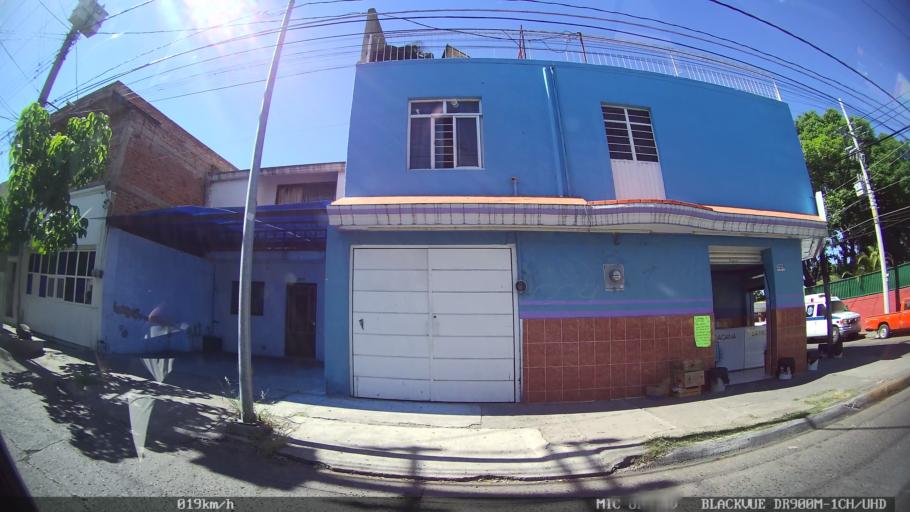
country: MX
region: Jalisco
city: Tlaquepaque
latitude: 20.6556
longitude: -103.2962
